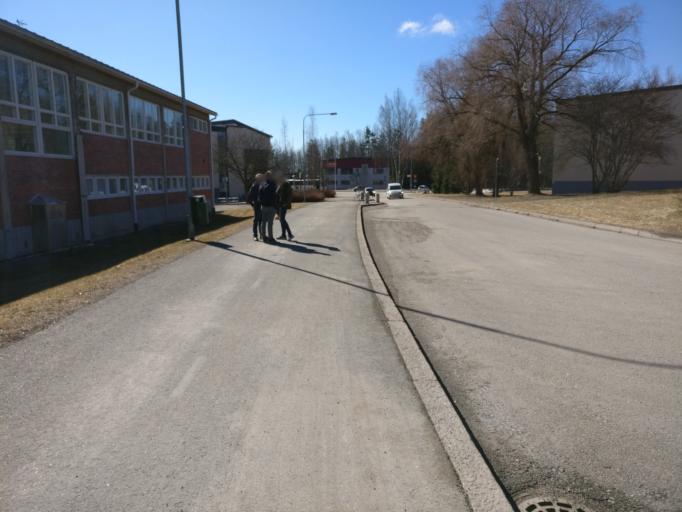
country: FI
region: Uusimaa
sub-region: Helsinki
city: Jaervenpaeae
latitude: 60.4818
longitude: 25.0813
